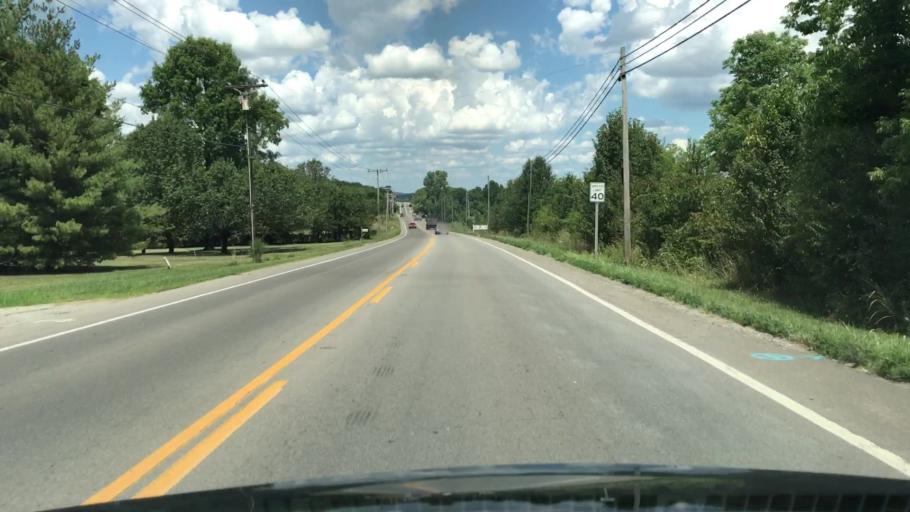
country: US
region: Tennessee
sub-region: Williamson County
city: Nolensville
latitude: 35.9388
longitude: -86.6615
